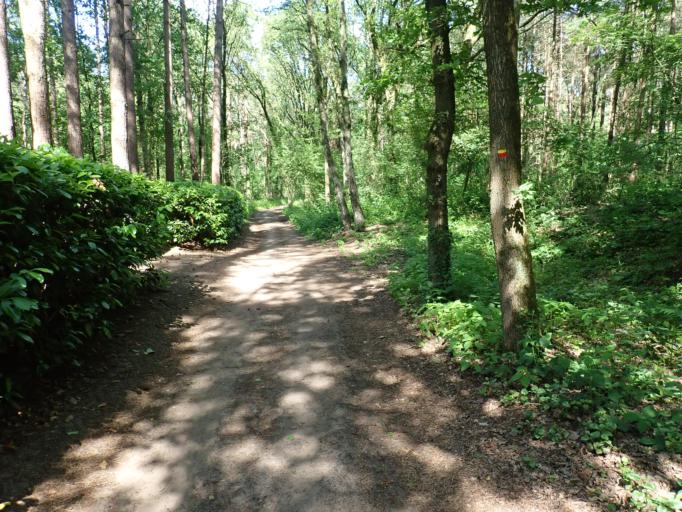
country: BE
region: Flanders
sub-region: Provincie Antwerpen
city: Kasterlee
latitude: 51.2240
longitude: 4.9368
